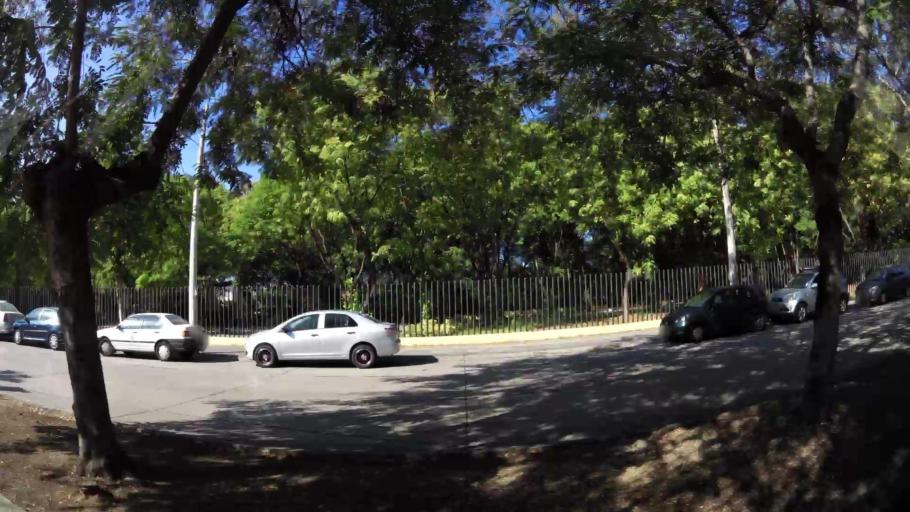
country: EC
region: Guayas
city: Guayaquil
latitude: -2.1651
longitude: -79.8988
